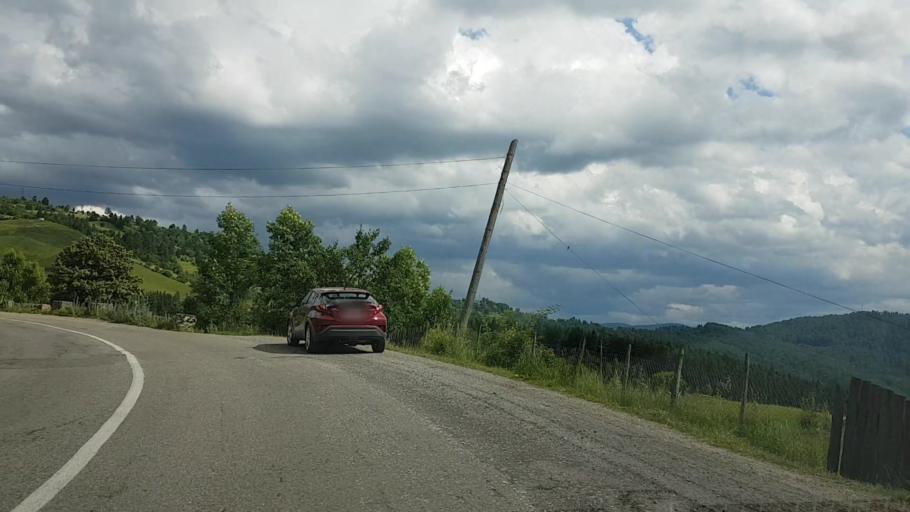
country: RO
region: Neamt
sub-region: Comuna Hangu
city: Hangu
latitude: 47.0075
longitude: 26.0901
